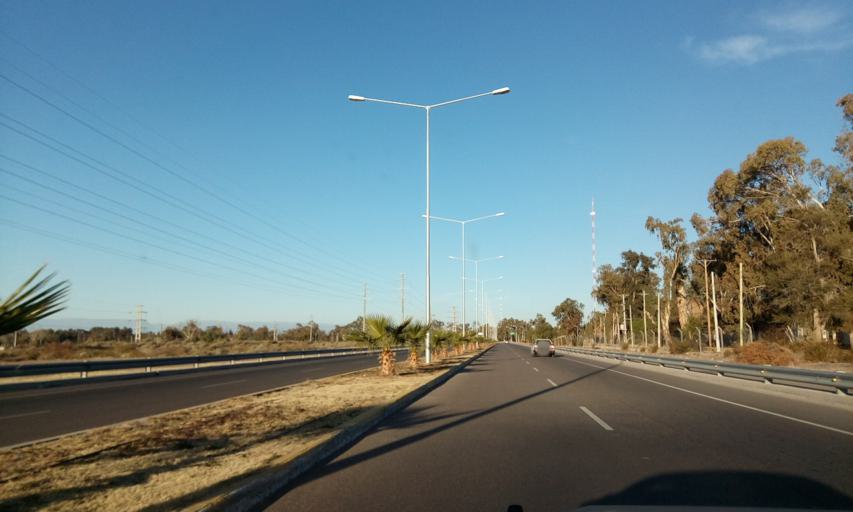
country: AR
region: San Juan
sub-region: Departamento de Rivadavia
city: Rivadavia
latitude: -31.5143
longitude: -68.6365
